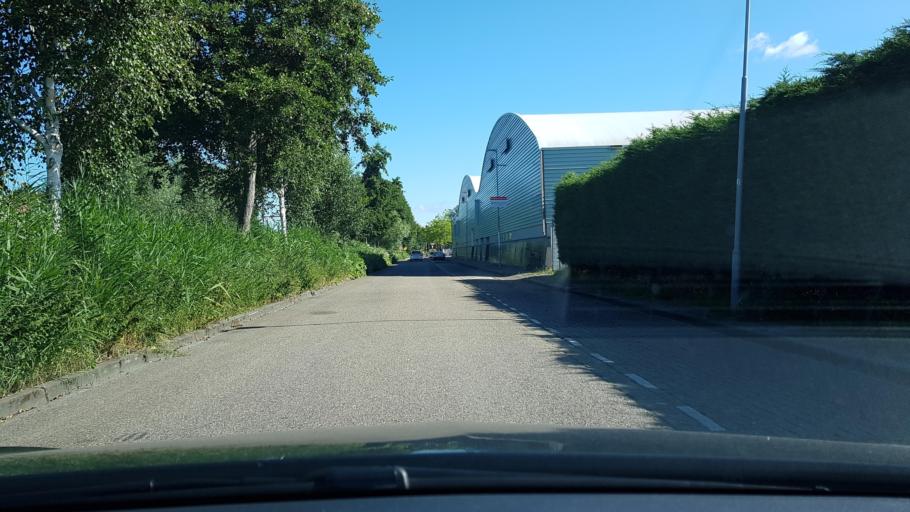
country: NL
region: North Holland
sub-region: Gemeente Bloemendaal
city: Bloemendaal
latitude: 52.3996
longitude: 4.6255
